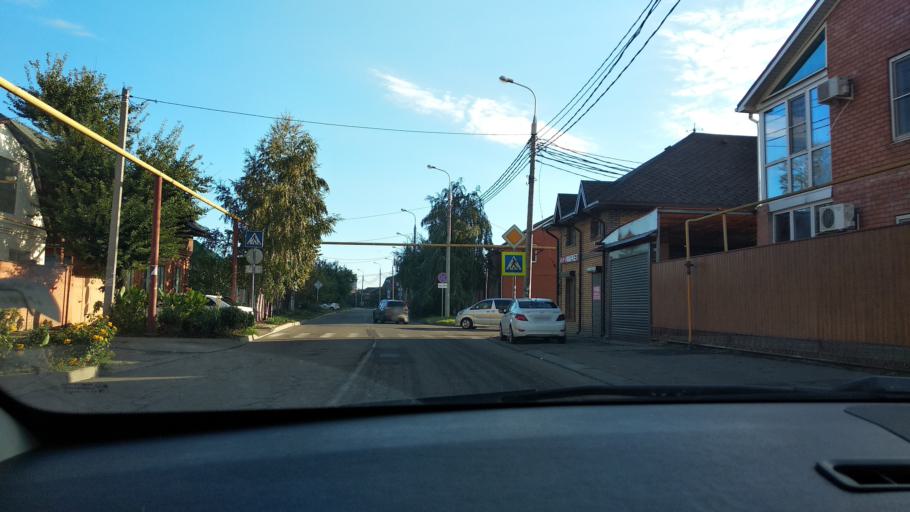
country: RU
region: Krasnodarskiy
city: Krasnodar
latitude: 45.0141
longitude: 38.9878
